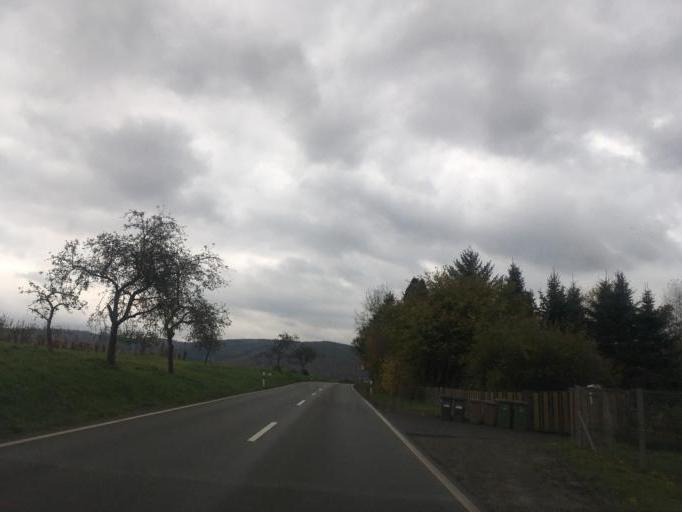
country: DE
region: Lower Saxony
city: Bodenfelde
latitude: 51.6175
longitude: 9.5520
